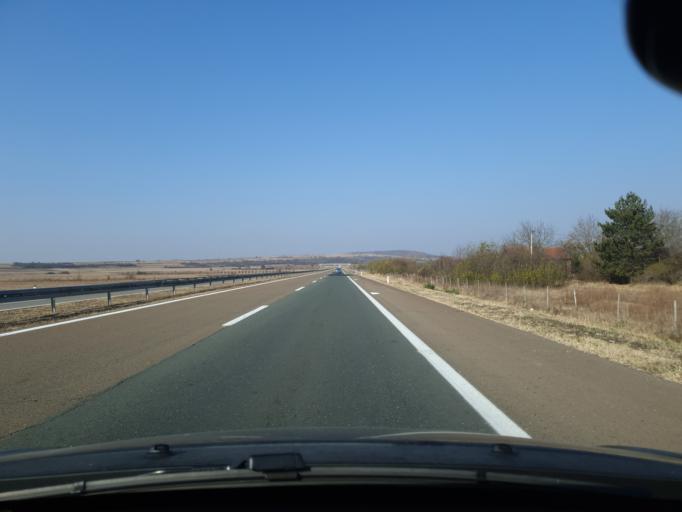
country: RS
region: Central Serbia
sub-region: Nisavski Okrug
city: Doljevac
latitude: 43.2279
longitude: 21.8291
